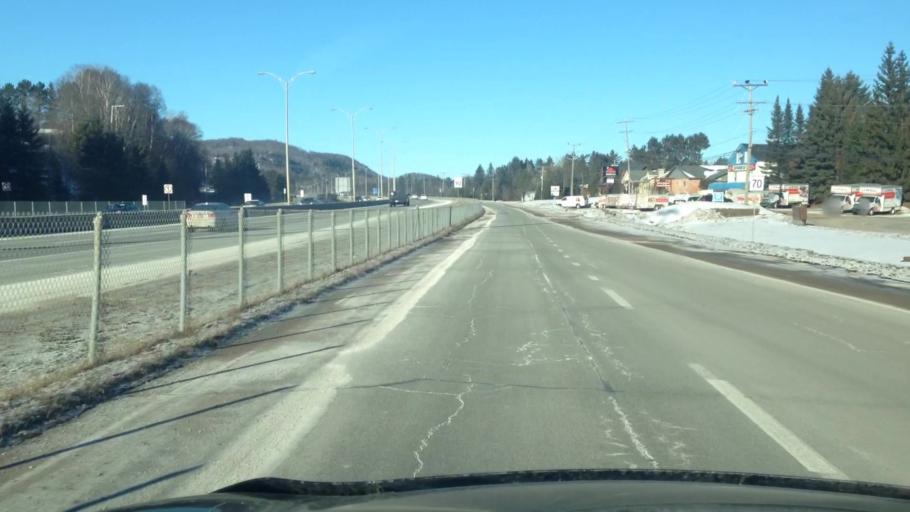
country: CA
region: Quebec
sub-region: Laurentides
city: Mont-Tremblant
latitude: 46.1208
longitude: -74.6074
